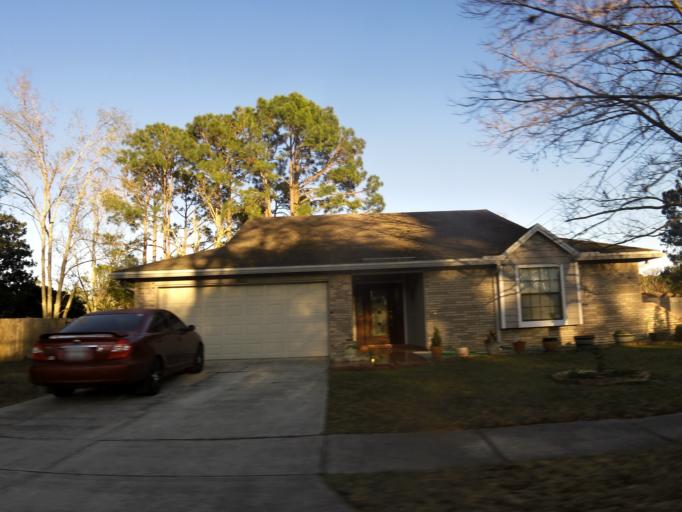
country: US
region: Florida
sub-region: Saint Johns County
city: Fruit Cove
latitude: 30.1725
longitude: -81.5795
